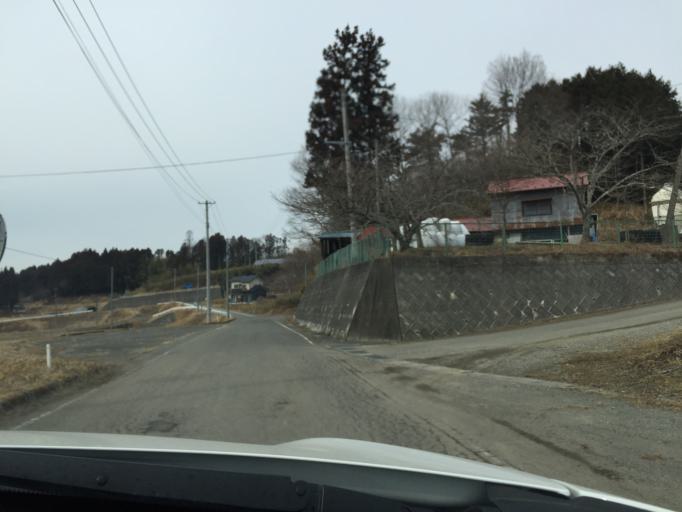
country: JP
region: Fukushima
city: Ishikawa
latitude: 37.2031
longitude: 140.5651
